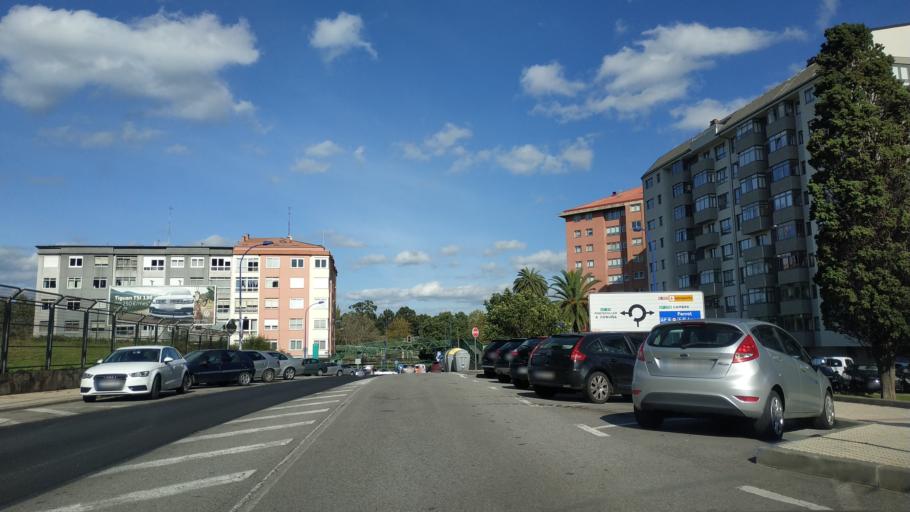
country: ES
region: Galicia
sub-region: Provincia da Coruna
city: Culleredo
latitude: 43.3175
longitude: -8.3730
